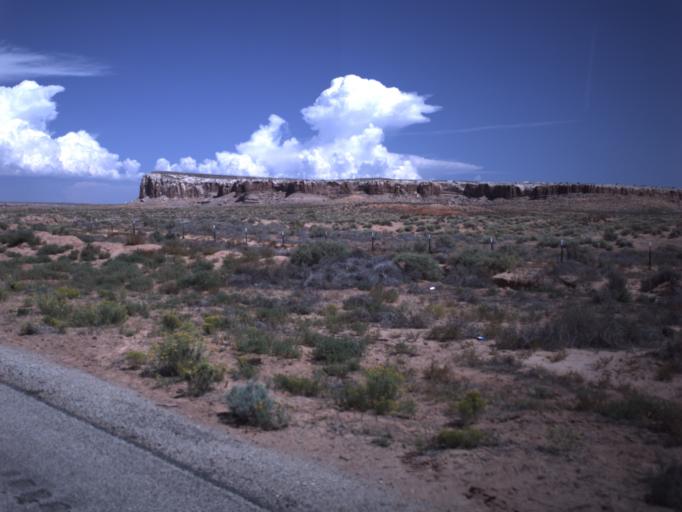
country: US
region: Utah
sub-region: San Juan County
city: Blanding
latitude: 37.2116
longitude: -109.6108
